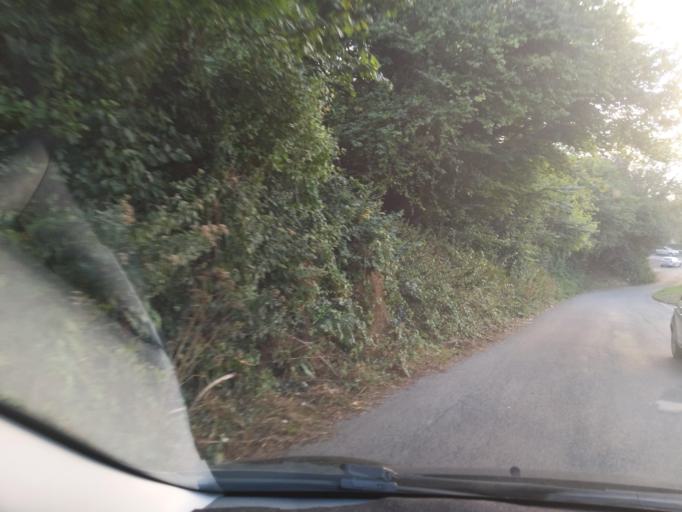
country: GB
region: England
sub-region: Plymouth
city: Plymstock
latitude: 50.3577
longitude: -4.0619
